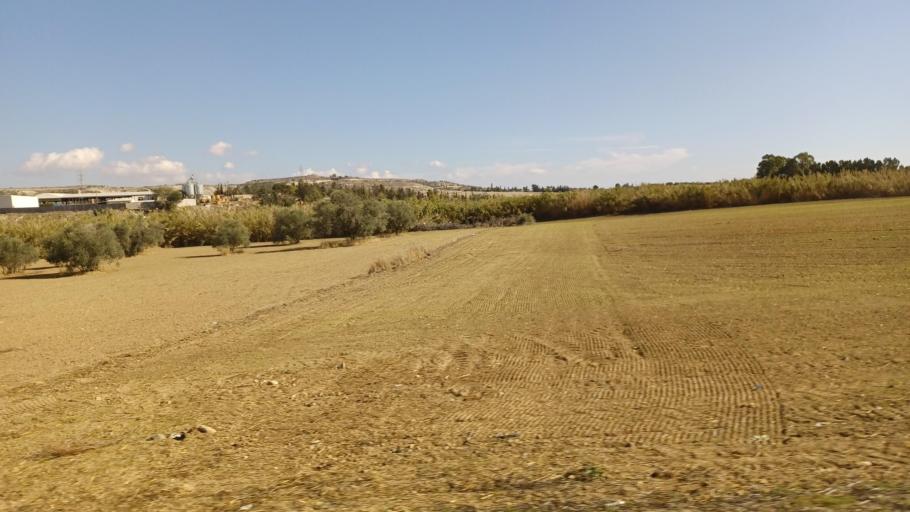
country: CY
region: Larnaka
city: Voroklini
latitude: 34.9995
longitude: 33.6522
